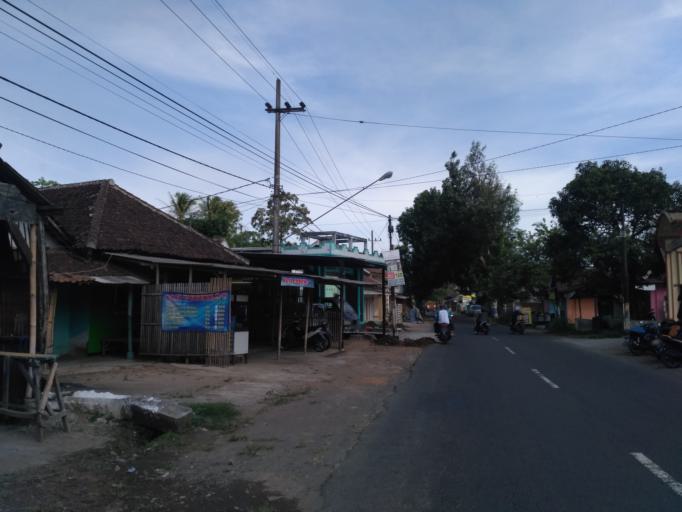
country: ID
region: East Java
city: Golek
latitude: -8.0668
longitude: 112.6264
